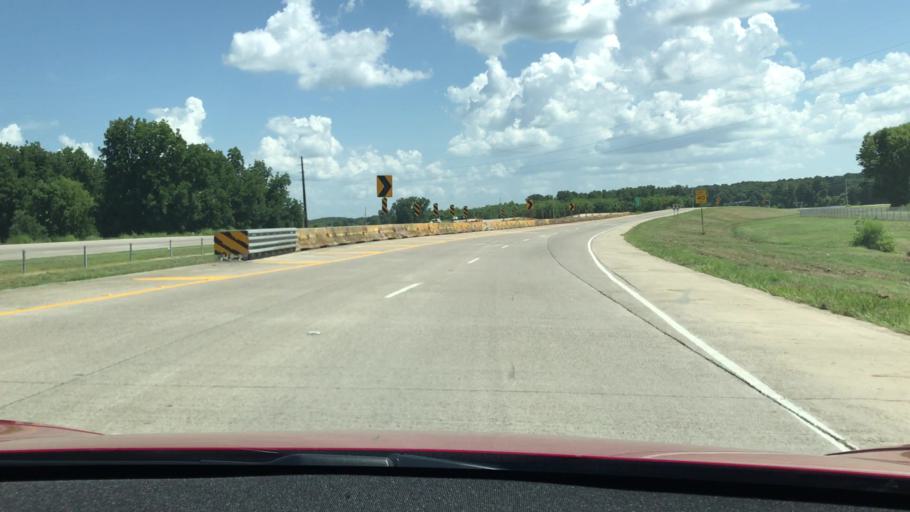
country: US
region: Louisiana
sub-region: Bossier Parish
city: Bossier City
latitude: 32.4054
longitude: -93.7149
